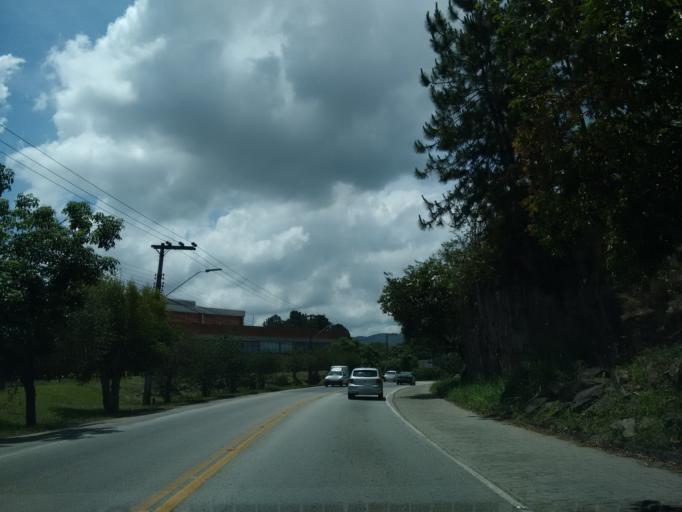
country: BR
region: Santa Catarina
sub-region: Blumenau
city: Blumenau
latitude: -26.9025
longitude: -49.0147
